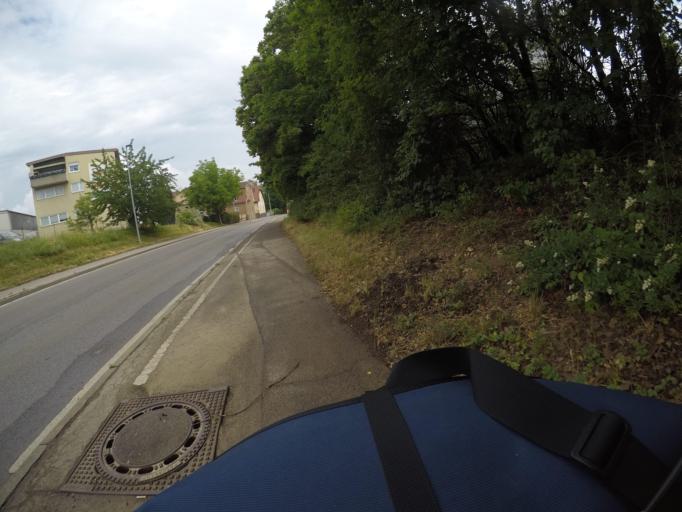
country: DE
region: Baden-Wuerttemberg
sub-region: Regierungsbezirk Stuttgart
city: Ditzingen
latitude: 48.8206
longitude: 9.0678
